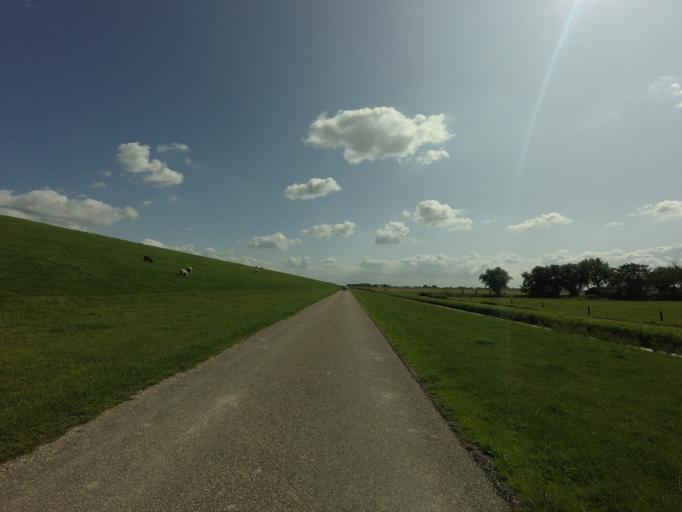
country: NL
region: Friesland
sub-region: Gemeente Ferwerderadiel
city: Hallum
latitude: 53.3223
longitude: 5.7426
